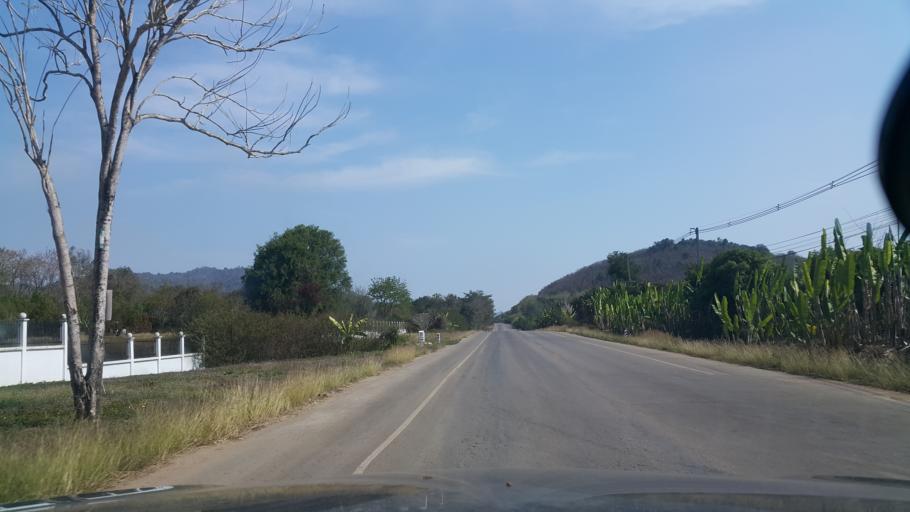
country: TH
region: Loei
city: Pak Chom
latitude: 18.1012
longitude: 101.9668
